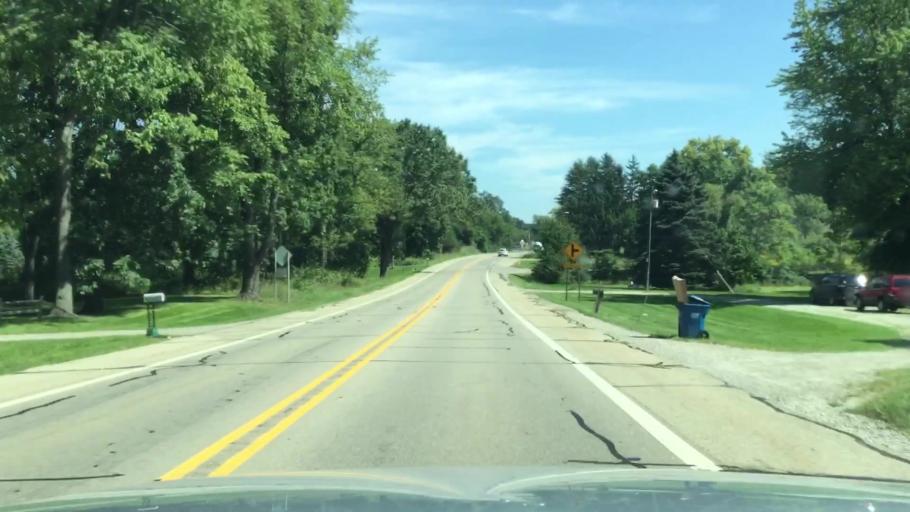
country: US
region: Michigan
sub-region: Washtenaw County
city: Manchester
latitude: 42.0646
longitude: -84.1086
